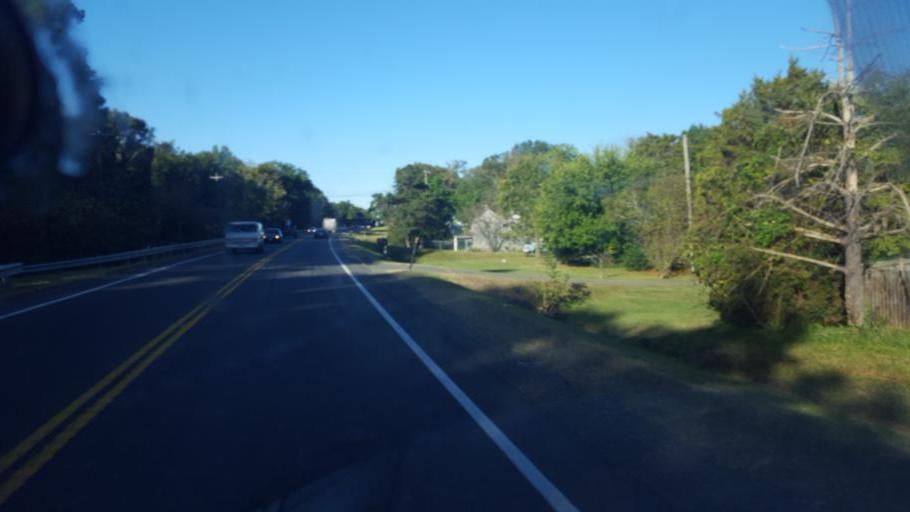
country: US
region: Virginia
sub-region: Prince William County
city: Nokesville
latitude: 38.6930
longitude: -77.5993
